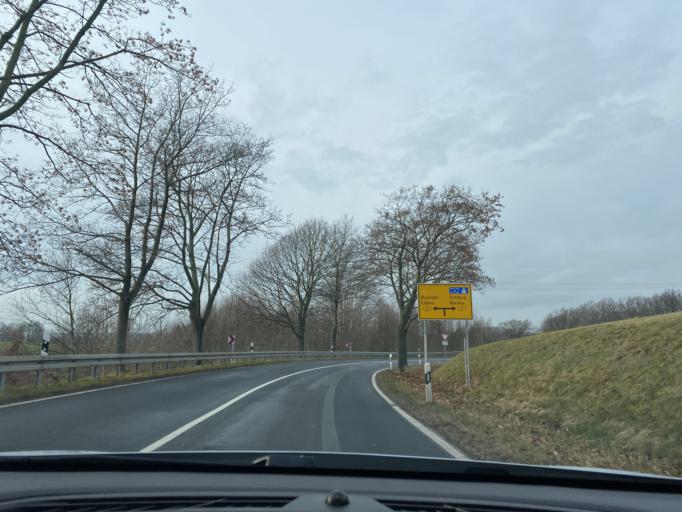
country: DE
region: Saxony
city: Markersdorf
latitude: 51.1470
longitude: 14.9174
